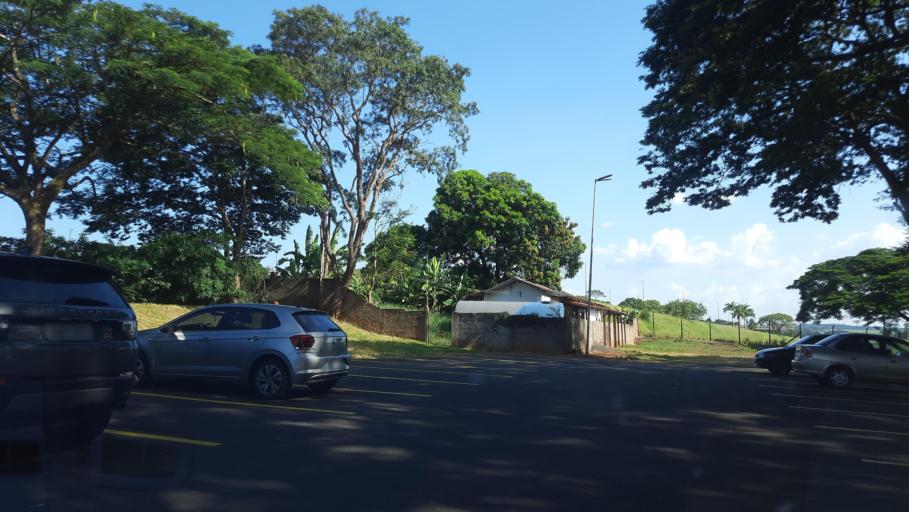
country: BR
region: Sao Paulo
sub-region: Jaguariuna
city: Jaguariuna
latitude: -22.7206
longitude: -47.0129
